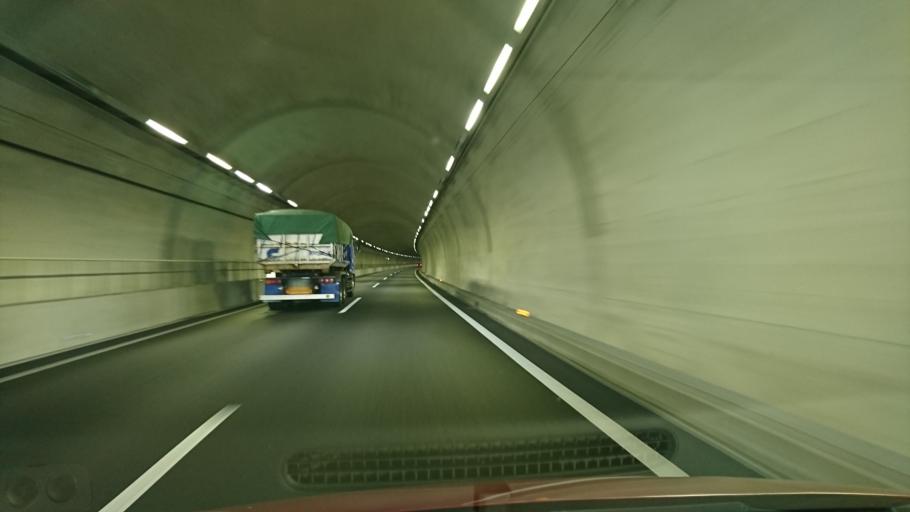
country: JP
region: Hyogo
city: Kawanishi
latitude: 34.8897
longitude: 135.3767
